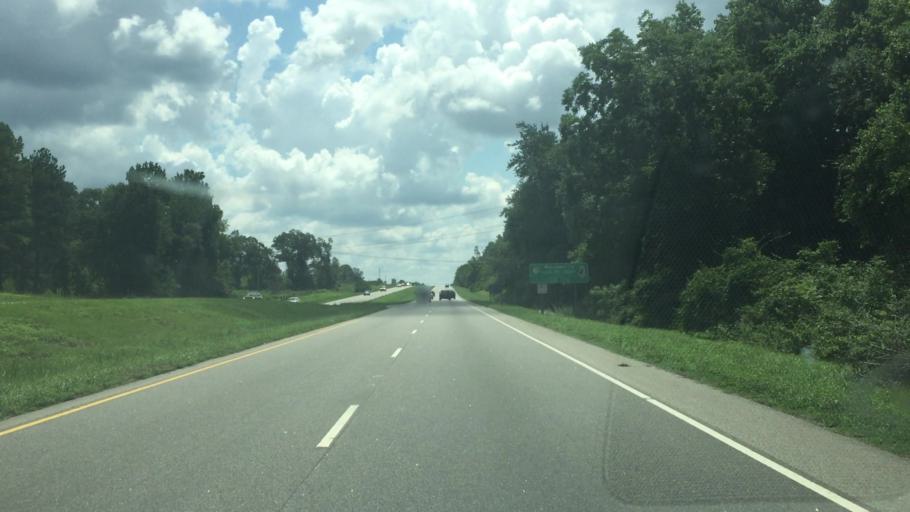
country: US
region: North Carolina
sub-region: Richmond County
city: Hamlet
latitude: 34.8543
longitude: -79.6231
